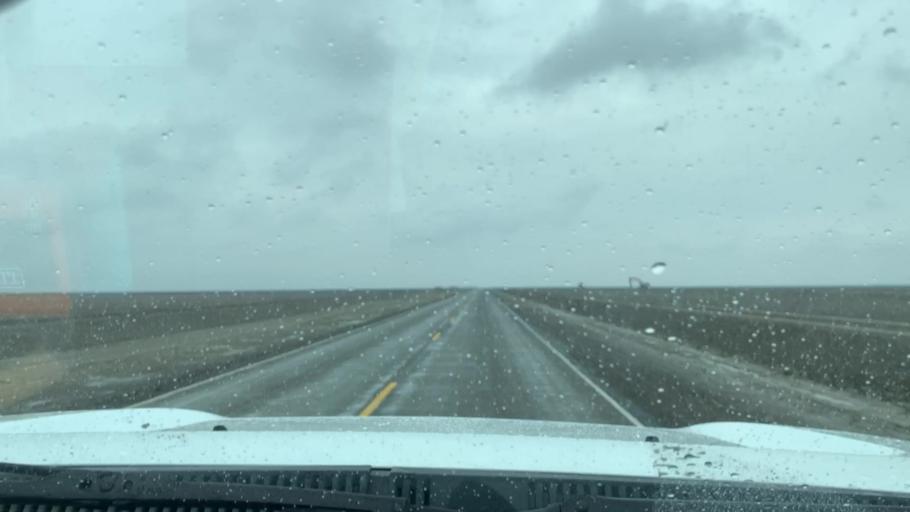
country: US
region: California
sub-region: Tulare County
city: Alpaugh
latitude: 35.9344
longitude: -119.5867
